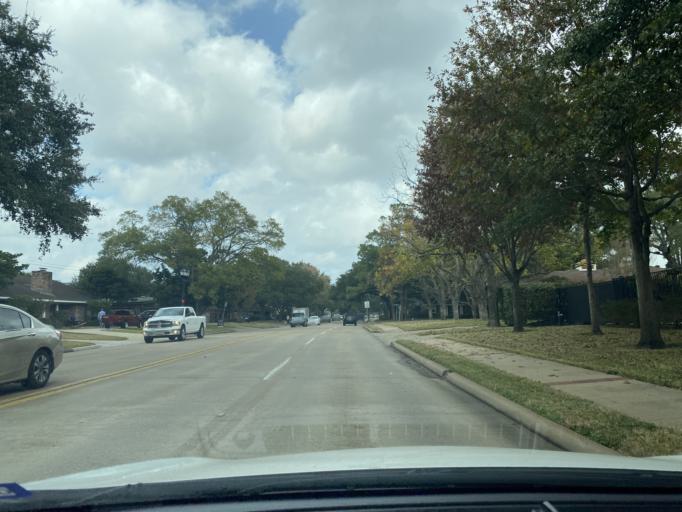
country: US
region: Texas
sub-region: Harris County
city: Hunters Creek Village
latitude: 29.7452
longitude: -95.4772
